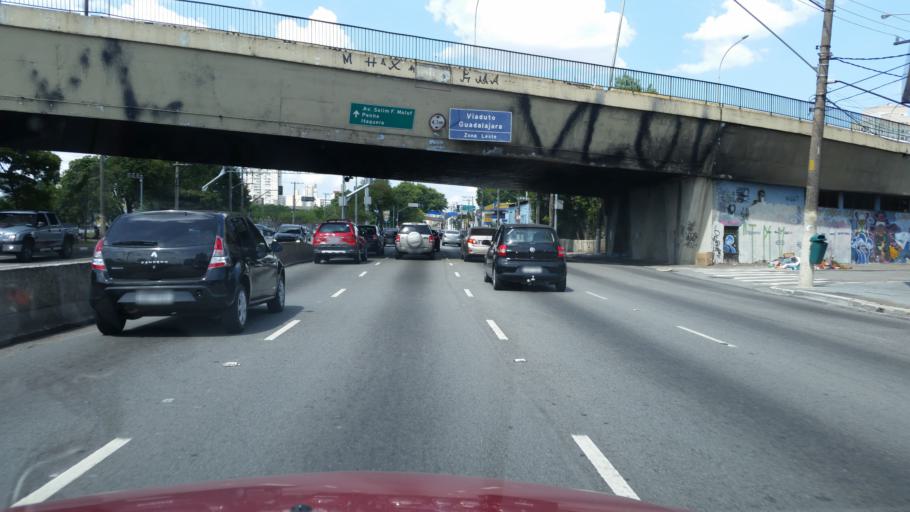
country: BR
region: Sao Paulo
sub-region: Sao Paulo
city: Sao Paulo
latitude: -23.5446
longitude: -46.5937
